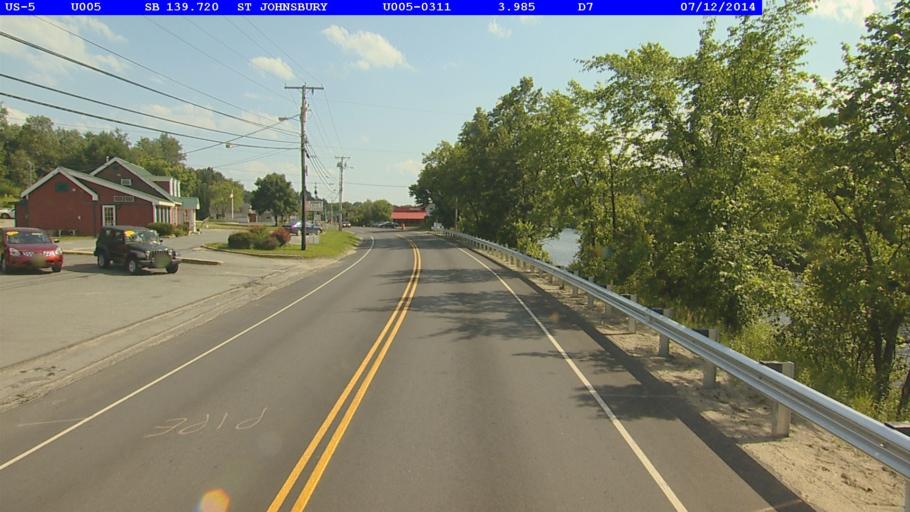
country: US
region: Vermont
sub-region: Caledonia County
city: St Johnsbury
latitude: 44.4488
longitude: -72.0159
